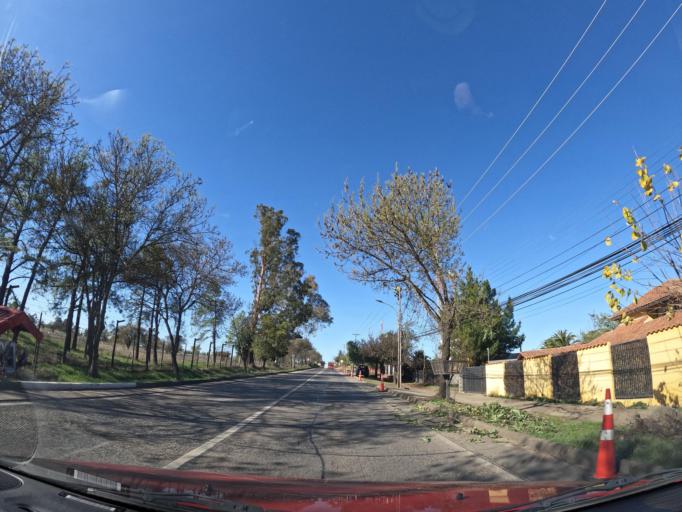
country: CL
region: Maule
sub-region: Provincia de Cauquenes
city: Cauquenes
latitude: -35.9574
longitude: -72.3028
